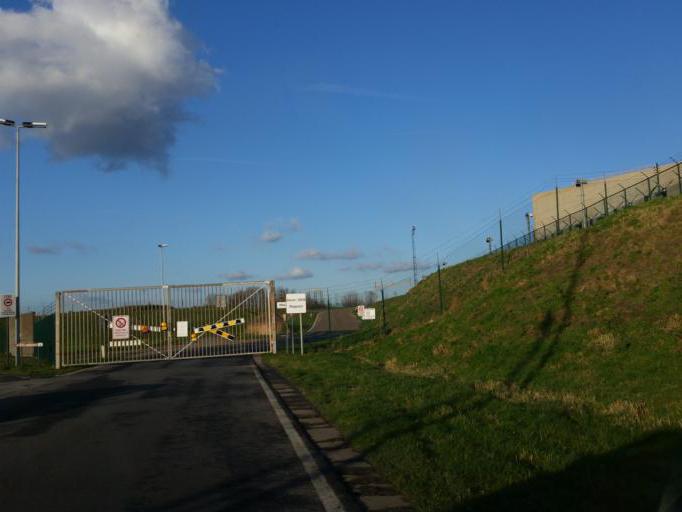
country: BE
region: Flanders
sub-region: Provincie Oost-Vlaanderen
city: Beveren
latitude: 51.3251
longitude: 4.2526
